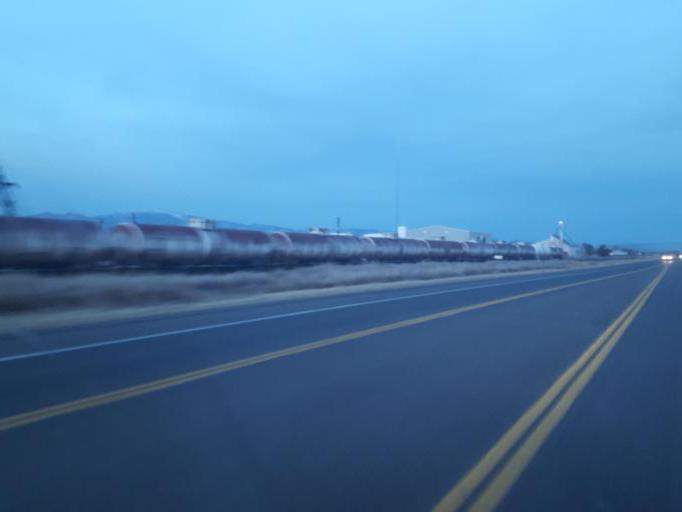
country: US
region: Colorado
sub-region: Rio Grande County
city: Monte Vista
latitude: 37.5610
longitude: -106.0972
